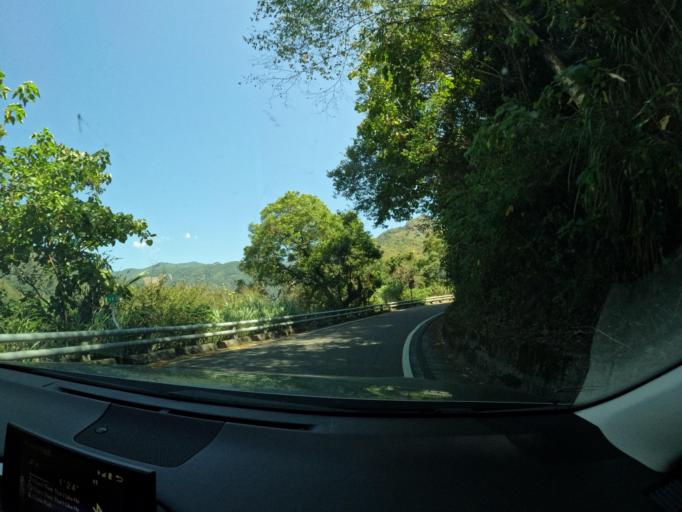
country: TW
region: Taiwan
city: Yujing
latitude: 23.2693
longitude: 120.8263
